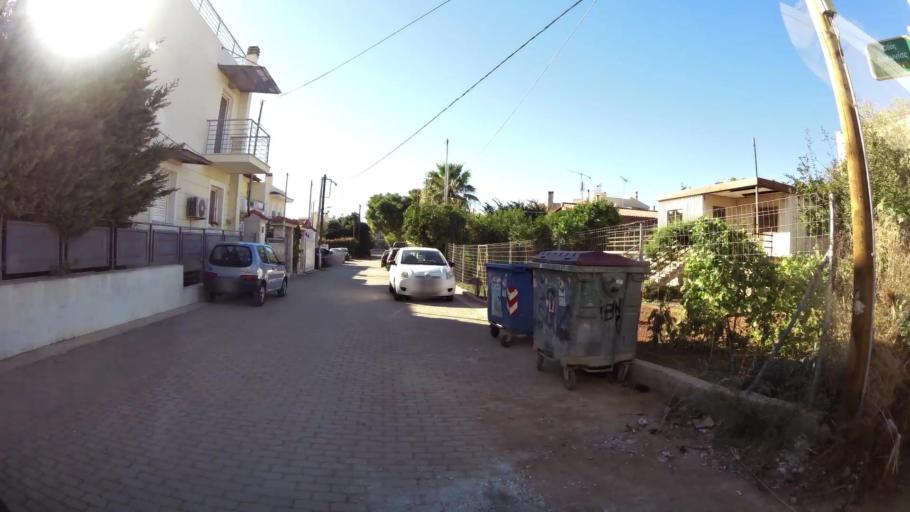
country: GR
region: Attica
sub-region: Nomarchia Anatolikis Attikis
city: Vari
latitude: 37.8355
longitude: 23.8122
